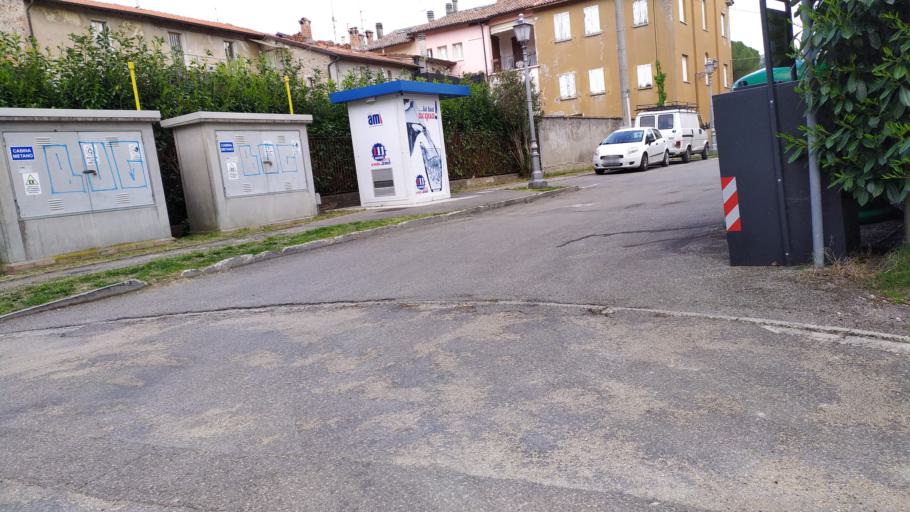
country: IT
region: Emilia-Romagna
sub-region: Provincia di Bologna
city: Borgo Tossignano
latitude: 44.2778
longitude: 11.5862
